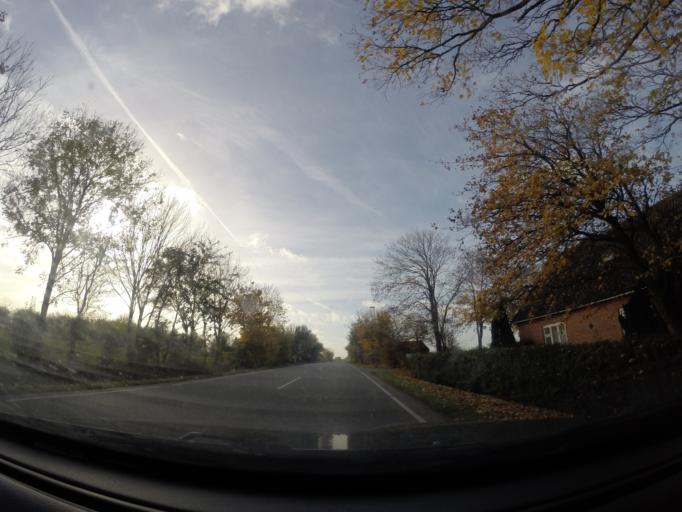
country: DK
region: South Denmark
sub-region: Faaborg-Midtfyn Kommune
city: Ringe
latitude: 55.1988
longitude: 10.5568
